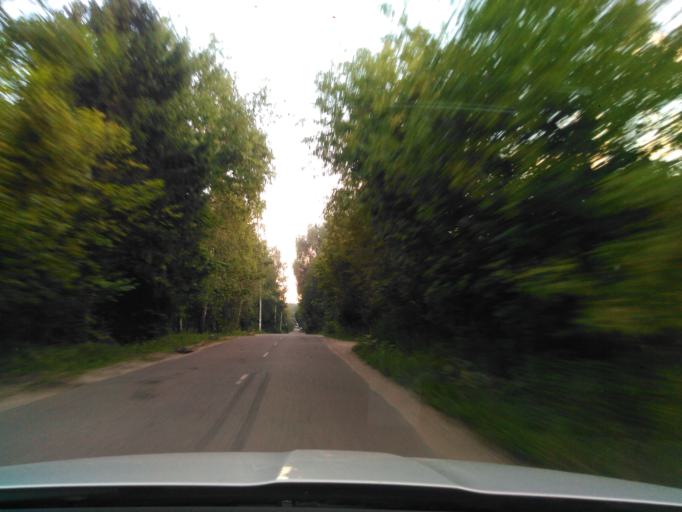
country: RU
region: Moskovskaya
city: Klin
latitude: 56.2229
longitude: 36.8056
